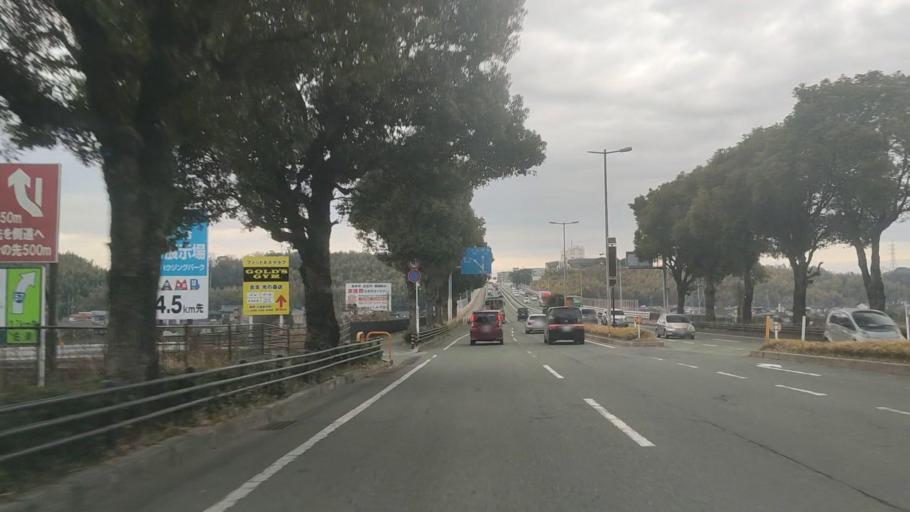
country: JP
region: Kumamoto
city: Ozu
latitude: 32.8459
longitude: 130.7815
